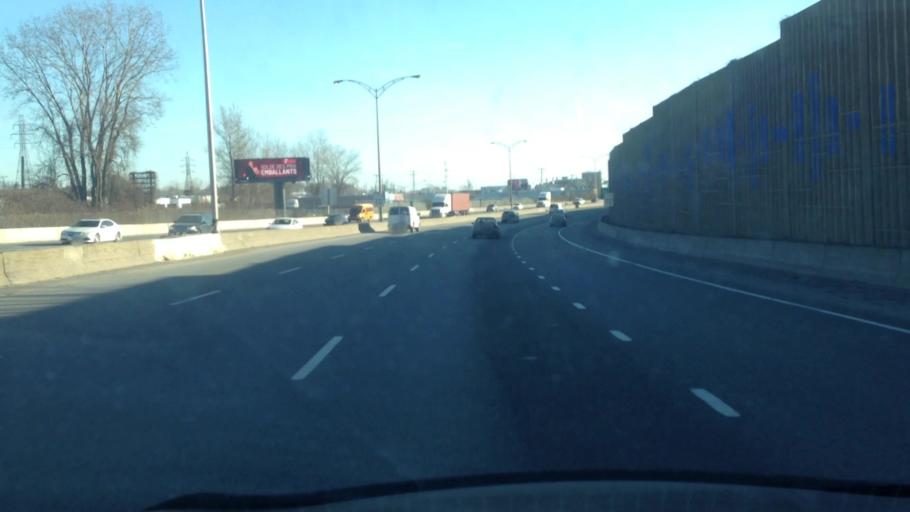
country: CA
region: Quebec
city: Cote-Saint-Luc
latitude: 45.4474
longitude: -73.6732
